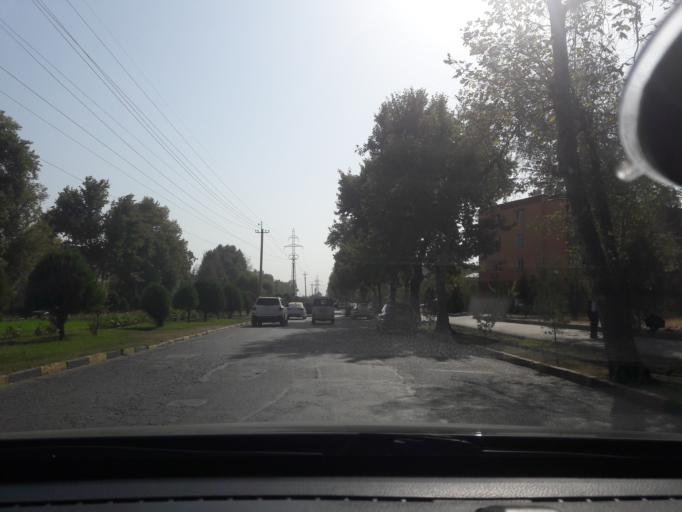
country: TJ
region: Dushanbe
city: Dushanbe
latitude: 38.5173
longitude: 68.7542
